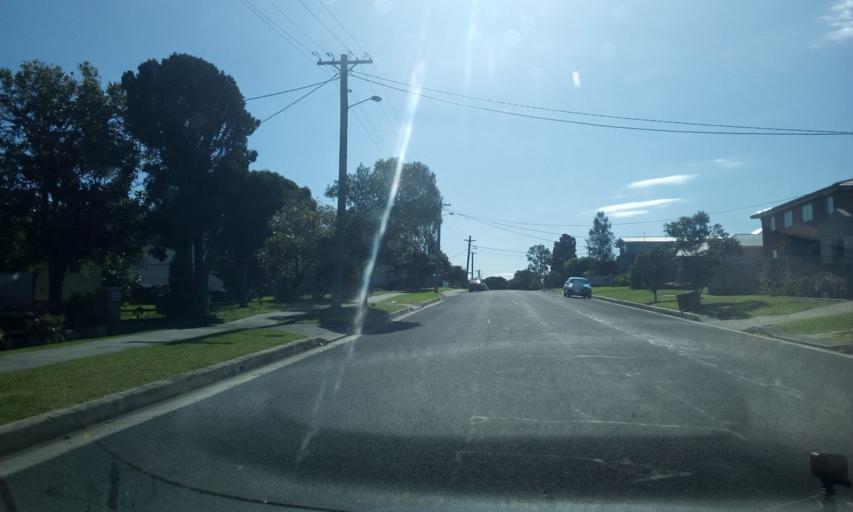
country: AU
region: New South Wales
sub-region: Wollongong
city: East Corrimal
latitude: -34.3700
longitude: 150.9082
